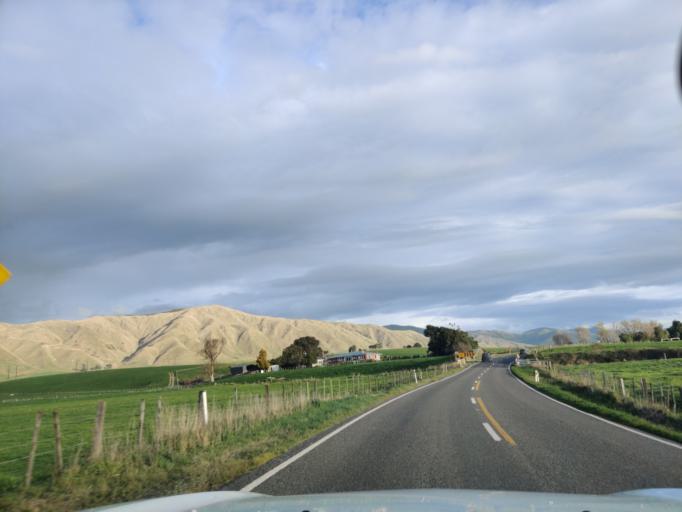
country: NZ
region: Manawatu-Wanganui
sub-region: Palmerston North City
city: Palmerston North
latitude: -40.4956
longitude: 175.4937
